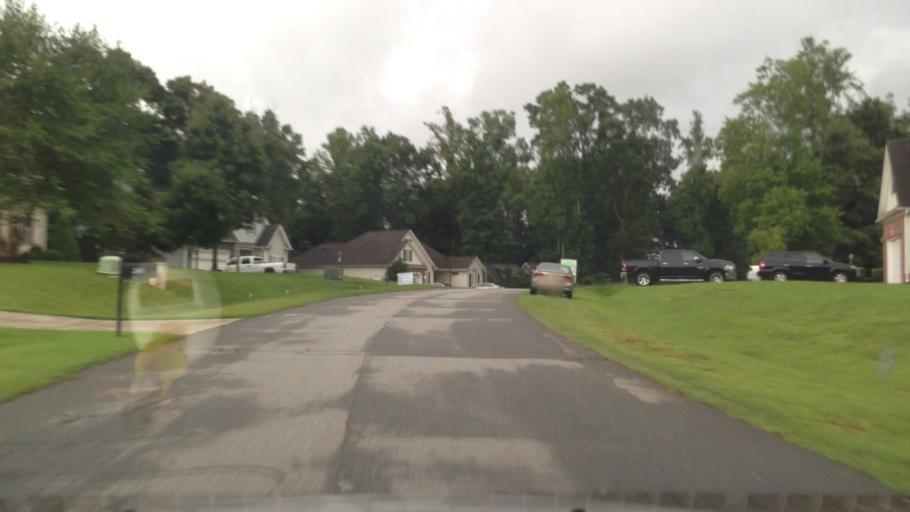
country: US
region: North Carolina
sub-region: Rockingham County
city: Reidsville
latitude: 36.2683
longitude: -79.7130
